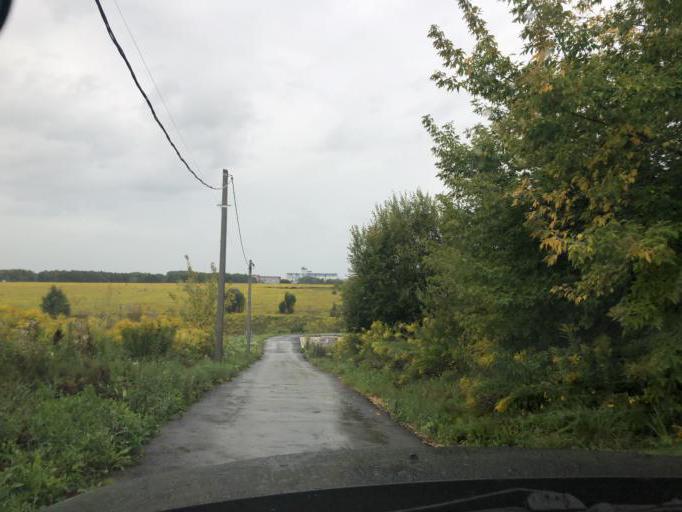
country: RU
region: Tula
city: Barsuki
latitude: 54.1989
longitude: 37.5156
